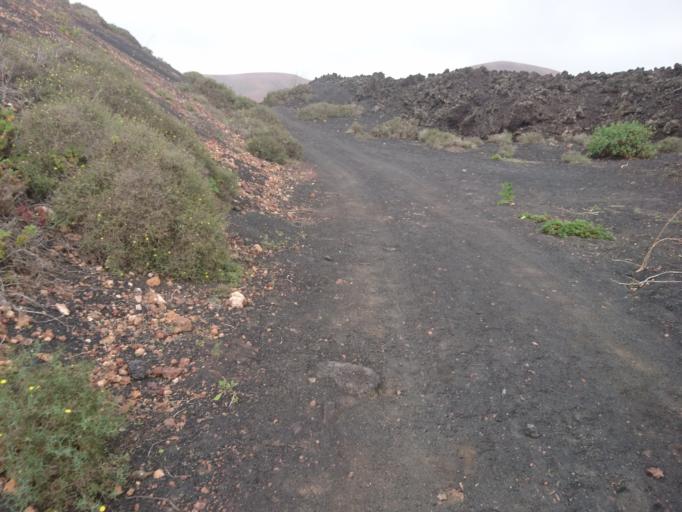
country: ES
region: Canary Islands
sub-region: Provincia de Las Palmas
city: Tinajo
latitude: 29.0145
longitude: -13.6922
